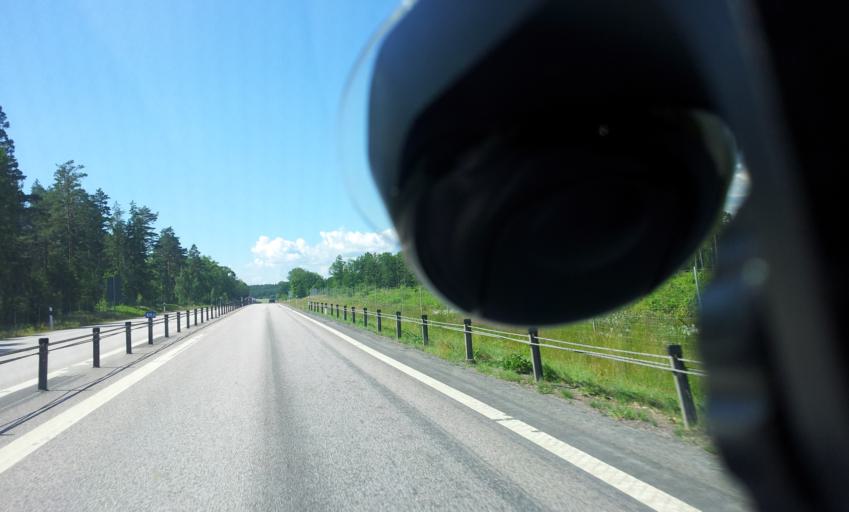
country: SE
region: Kalmar
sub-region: Monsteras Kommun
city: Moensteras
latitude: 57.0987
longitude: 16.4935
